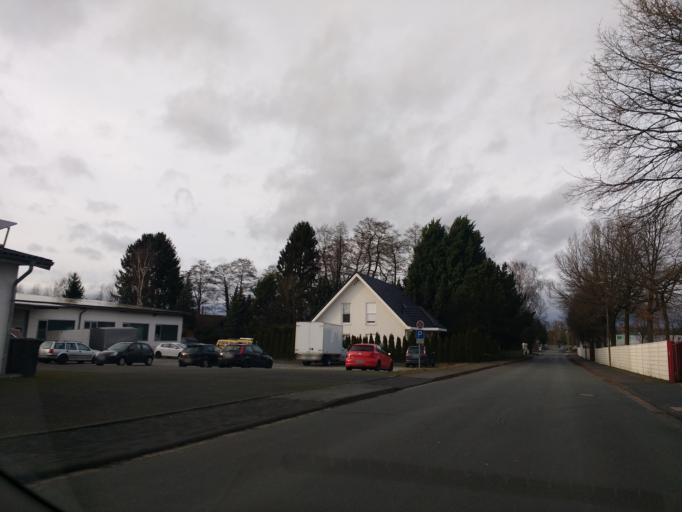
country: DE
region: North Rhine-Westphalia
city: Bad Lippspringe
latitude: 51.7779
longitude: 8.7971
